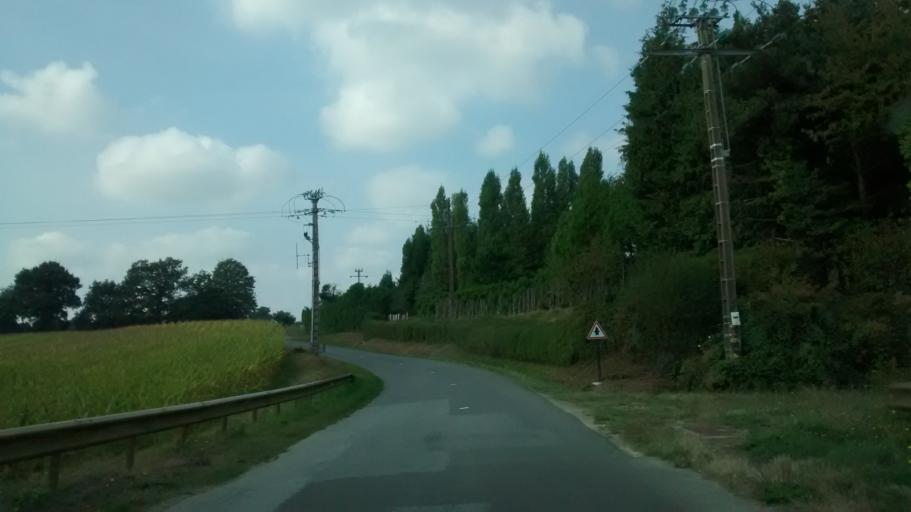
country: FR
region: Brittany
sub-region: Departement d'Ille-et-Vilaine
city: Montreuil-sous-Perouse
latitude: 48.2254
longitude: -1.2557
